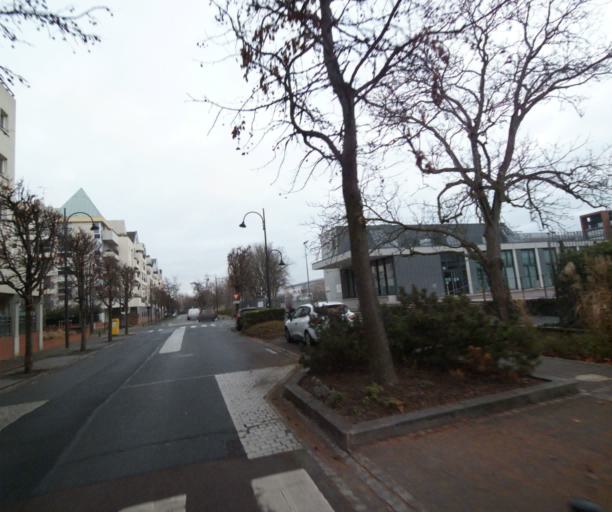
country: FR
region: Ile-de-France
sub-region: Departement des Yvelines
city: Chatou
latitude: 48.8918
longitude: 2.1691
